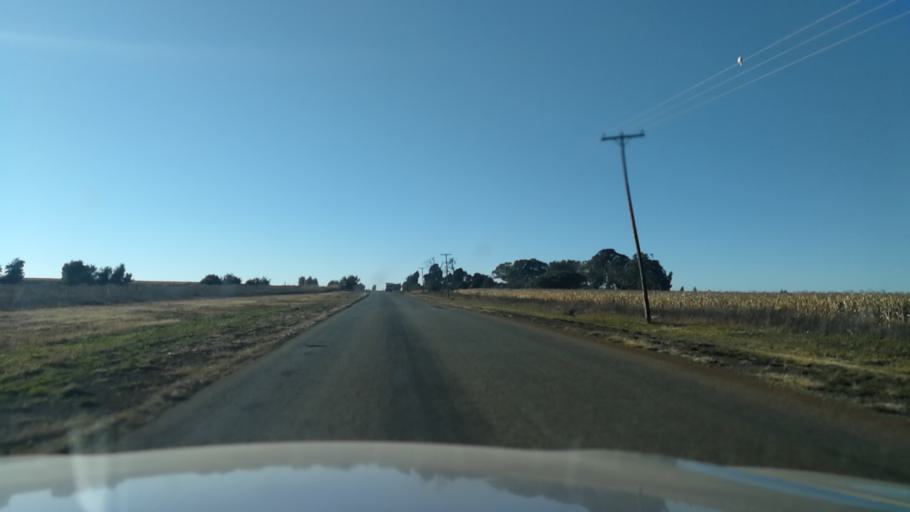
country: ZA
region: North-West
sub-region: Bojanala Platinum District Municipality
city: Rustenburg
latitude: -25.9778
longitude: 27.2538
